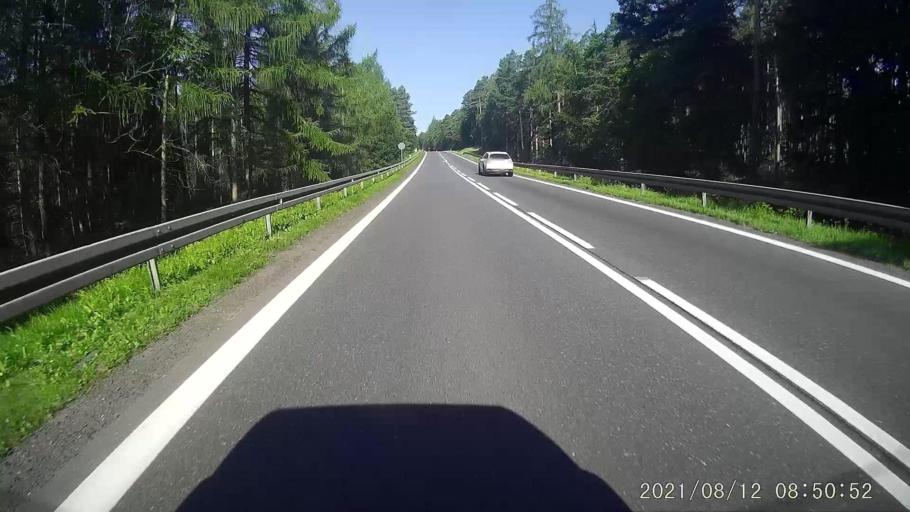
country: PL
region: Lower Silesian Voivodeship
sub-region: Powiat klodzki
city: Polanica-Zdroj
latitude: 50.4243
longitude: 16.4892
